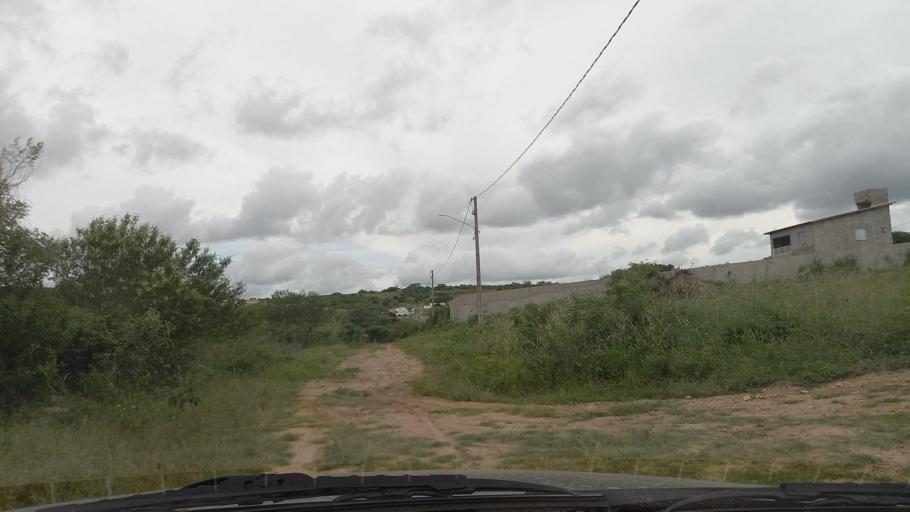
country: BR
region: Pernambuco
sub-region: Gravata
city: Gravata
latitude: -8.2260
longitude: -35.5748
